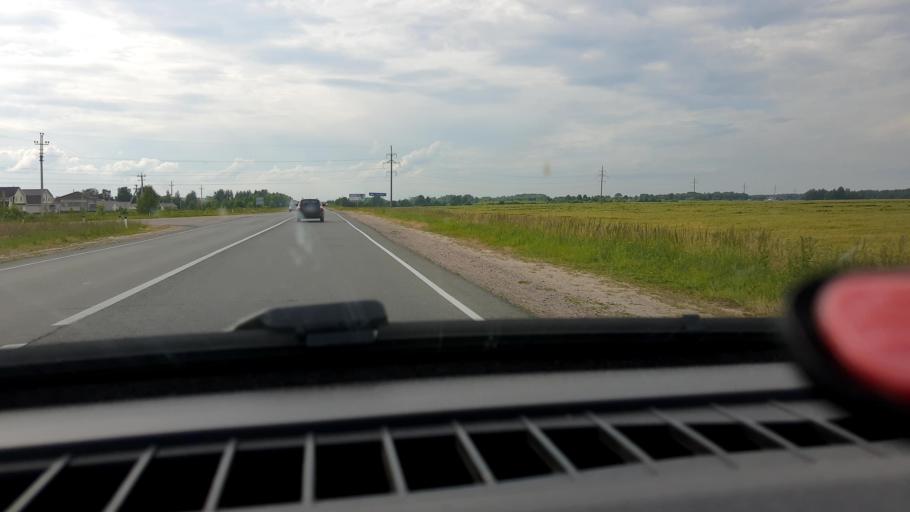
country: RU
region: Nizjnij Novgorod
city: Gorodets
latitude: 56.6650
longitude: 43.4931
